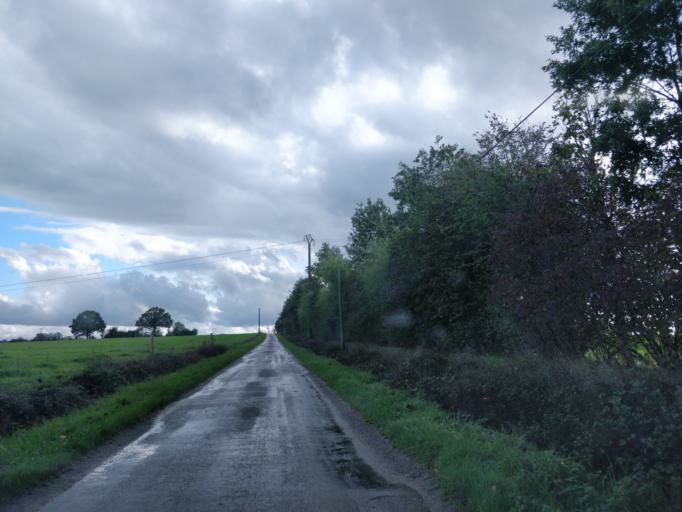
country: FR
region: Brittany
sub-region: Departement d'Ille-et-Vilaine
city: Chateaubourg
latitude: 48.1280
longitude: -1.4257
